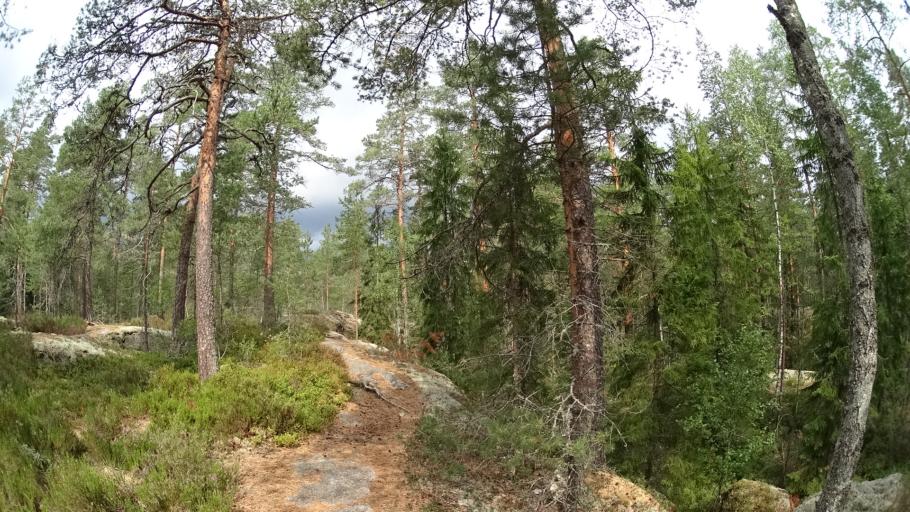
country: FI
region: Uusimaa
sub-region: Helsinki
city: Espoo
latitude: 60.3053
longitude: 24.5798
